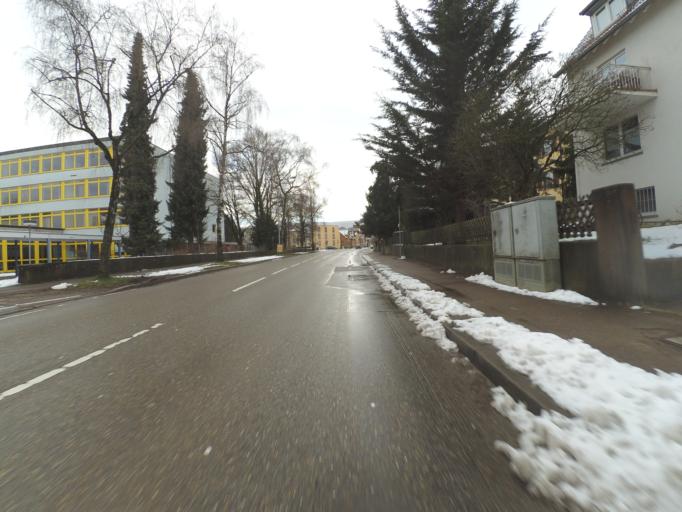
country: DE
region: Baden-Wuerttemberg
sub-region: Regierungsbezirk Stuttgart
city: Aalen
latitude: 48.8417
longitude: 10.0888
